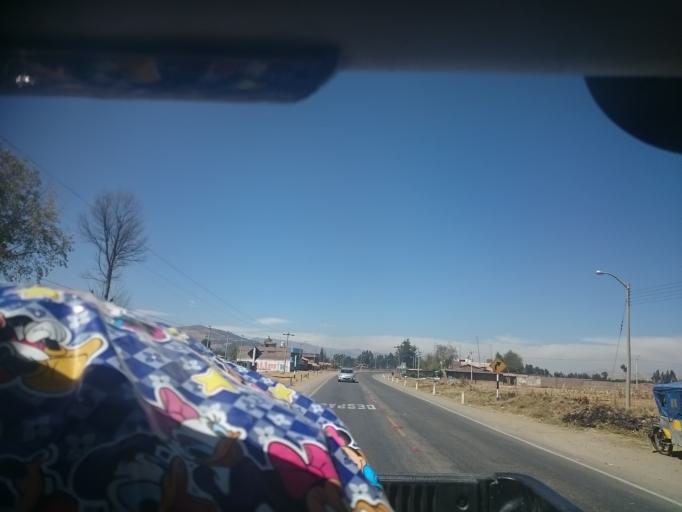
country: PE
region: Junin
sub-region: Provincia de Jauja
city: San Lorenzo
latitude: -11.8348
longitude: -75.3955
